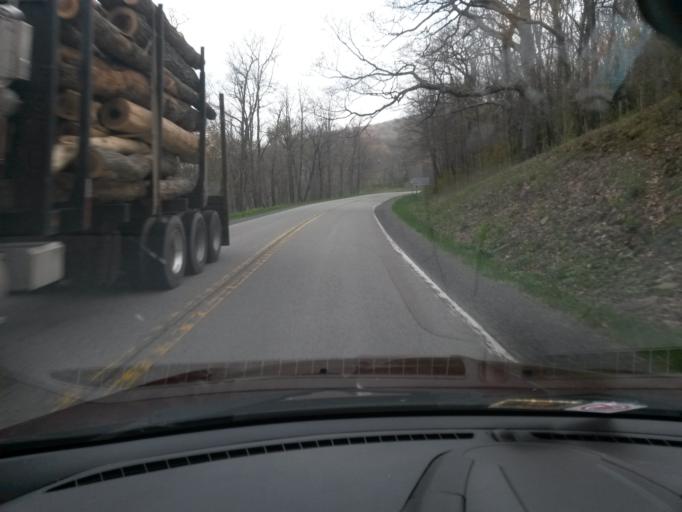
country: US
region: Virginia
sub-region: Highland County
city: Monterey
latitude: 38.4759
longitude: -79.6990
